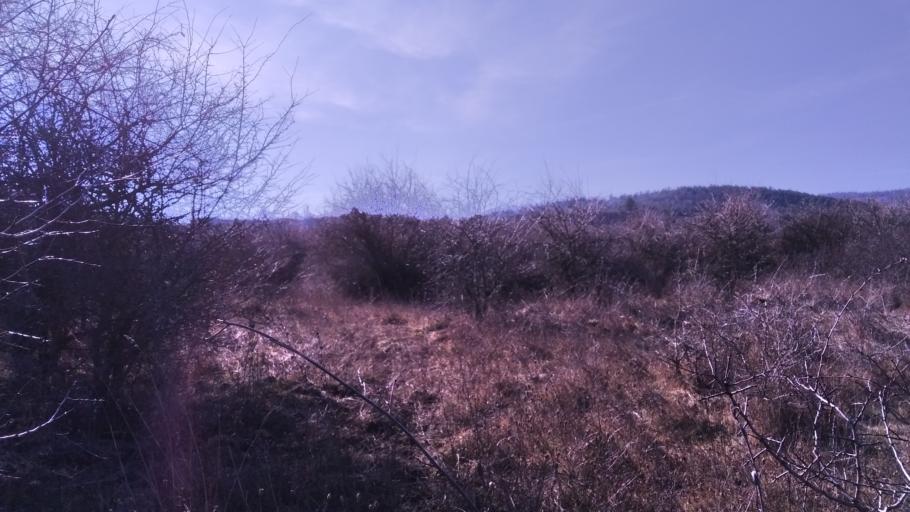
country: HU
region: Pest
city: Pomaz
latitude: 47.6253
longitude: 19.0178
